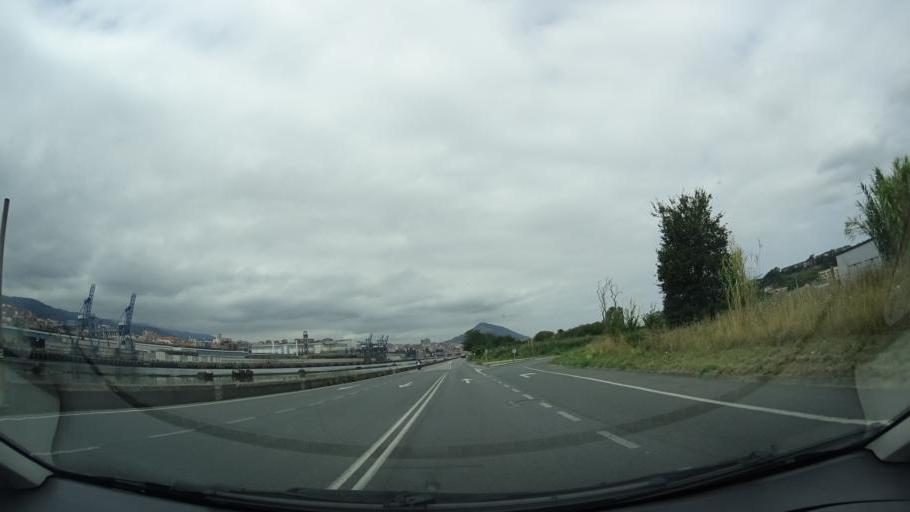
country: ES
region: Basque Country
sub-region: Bizkaia
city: Sestao
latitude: 43.3157
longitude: -2.9929
